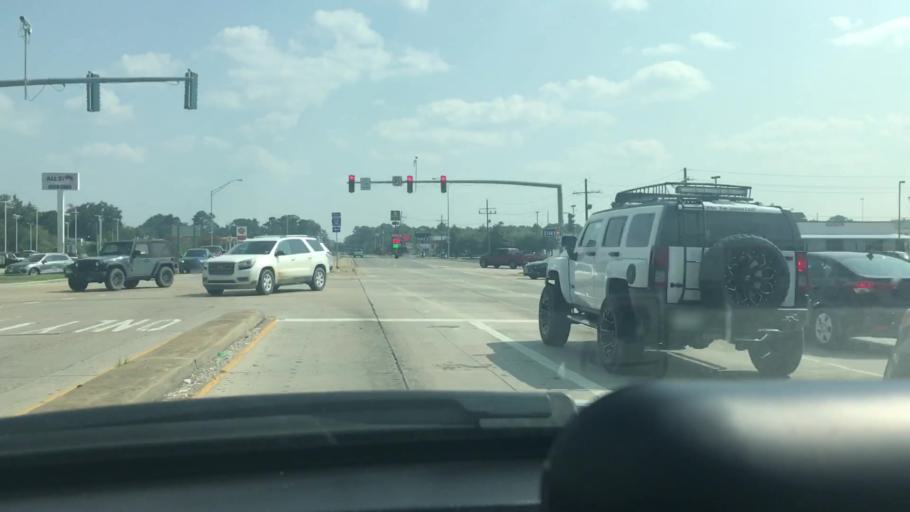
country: US
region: Louisiana
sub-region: Livingston Parish
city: Denham Springs
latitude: 30.4546
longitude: -90.9566
